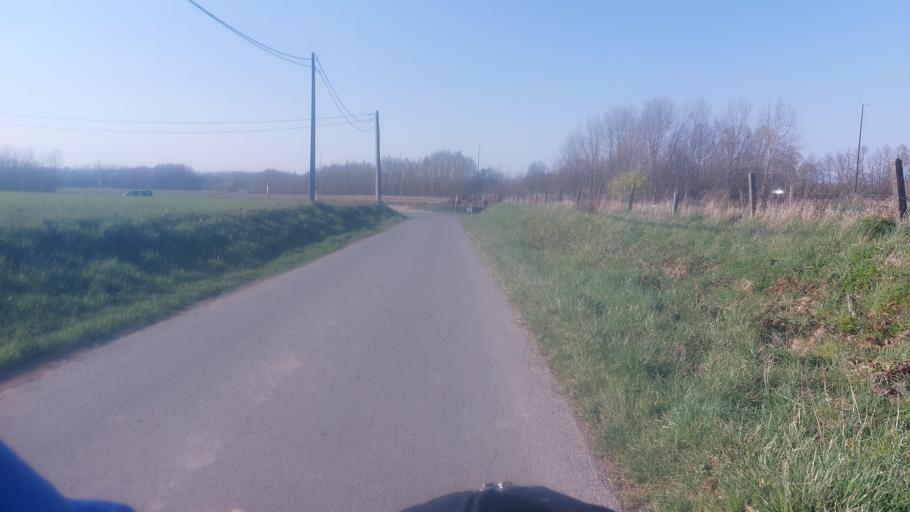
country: BE
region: Wallonia
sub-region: Province du Hainaut
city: Lessines
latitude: 50.6736
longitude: 3.8371
